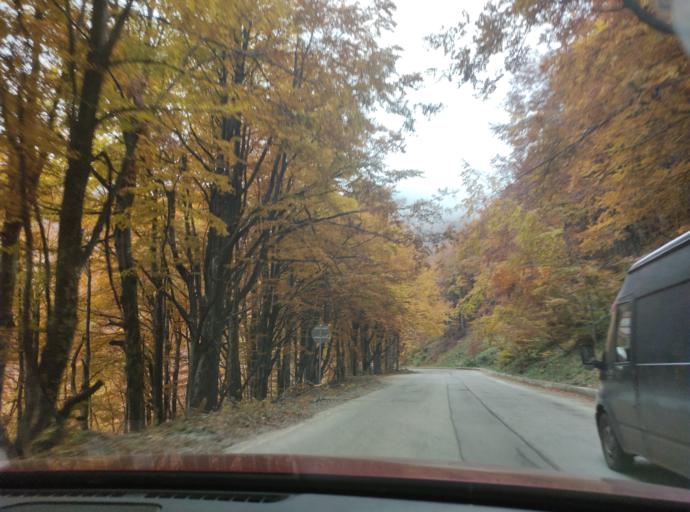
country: BG
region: Montana
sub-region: Obshtina Berkovitsa
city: Berkovitsa
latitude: 43.1234
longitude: 23.1362
